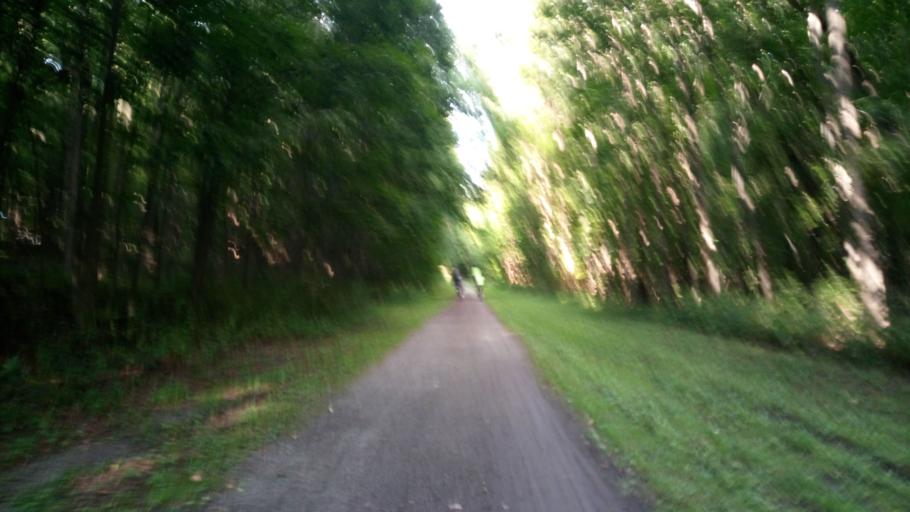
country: US
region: New York
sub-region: Monroe County
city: Honeoye Falls
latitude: 42.9941
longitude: -77.5179
